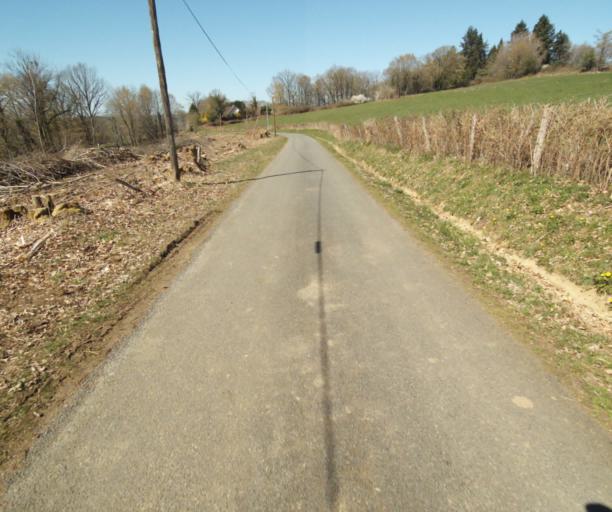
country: FR
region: Limousin
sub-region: Departement de la Correze
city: Uzerche
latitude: 45.4033
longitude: 1.6249
